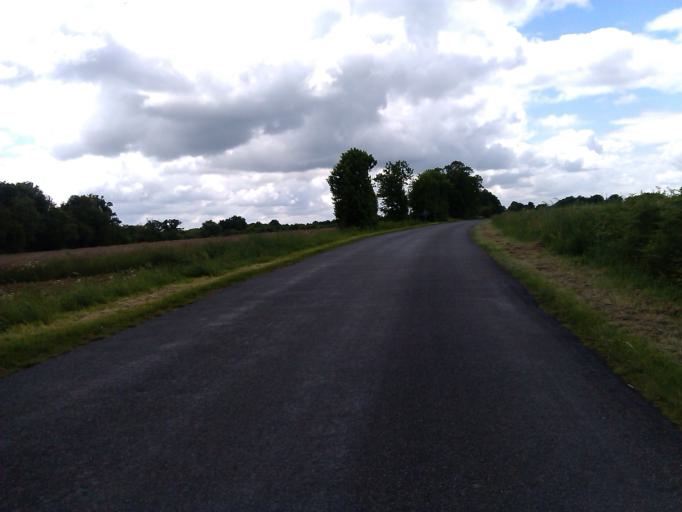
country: FR
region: Poitou-Charentes
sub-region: Departement de la Charente
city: Champagne-Mouton
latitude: 46.0207
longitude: 0.4390
